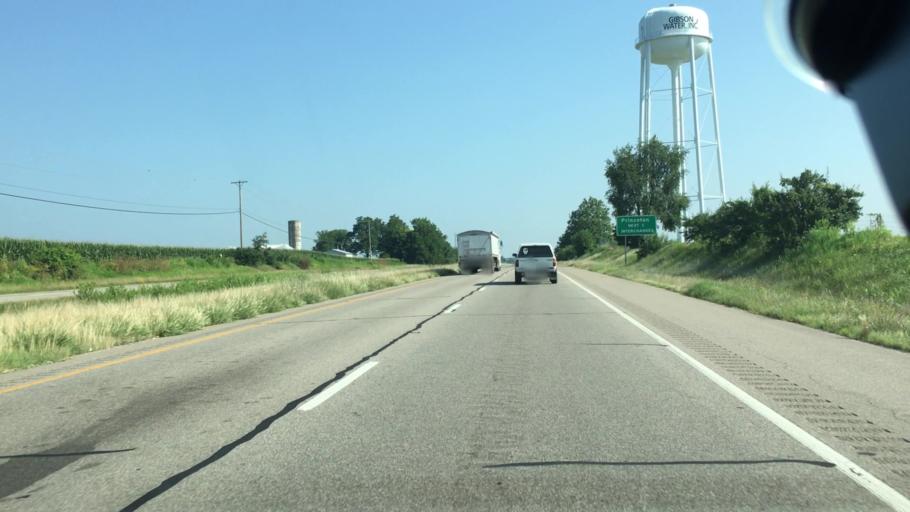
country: US
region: Indiana
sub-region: Gibson County
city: Fort Branch
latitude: 38.2889
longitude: -87.5674
